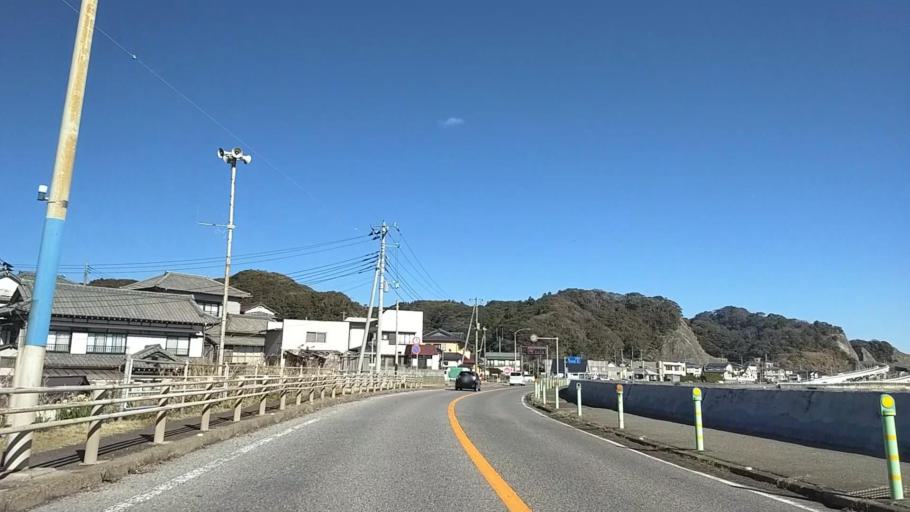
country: JP
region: Chiba
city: Katsuura
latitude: 35.1503
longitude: 140.2965
